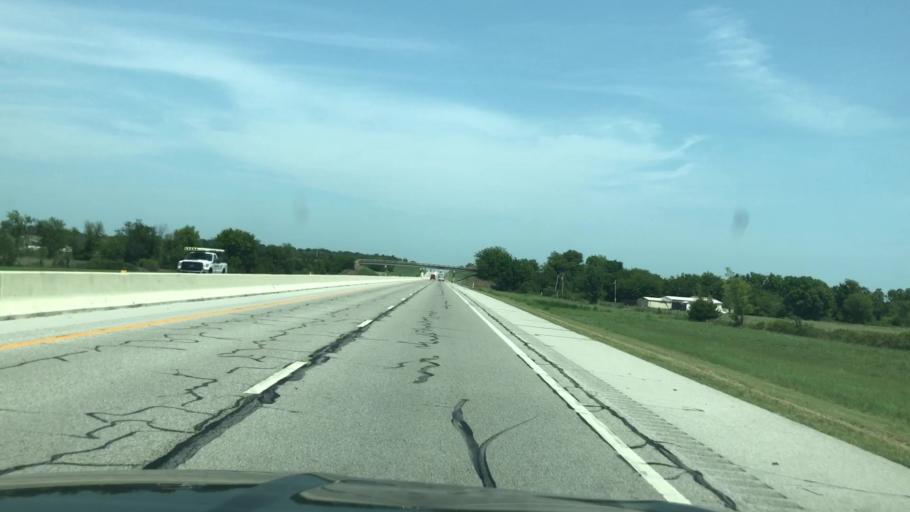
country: US
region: Oklahoma
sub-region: Rogers County
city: Chelsea
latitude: 36.4796
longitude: -95.3177
